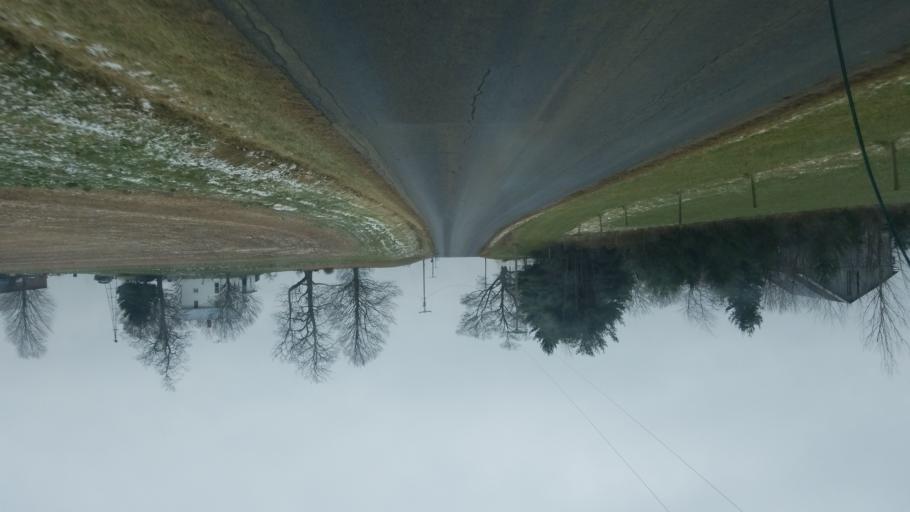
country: US
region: Ohio
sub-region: Huron County
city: Greenwich
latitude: 40.9756
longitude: -82.5238
